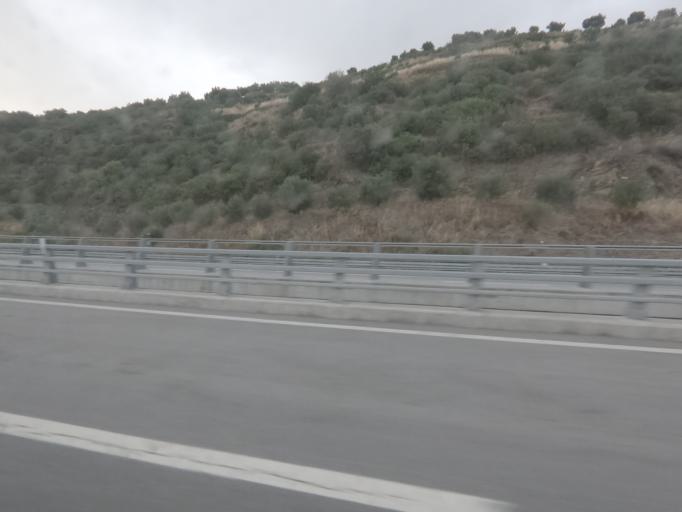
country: PT
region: Vila Real
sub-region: Peso da Regua
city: Peso da Regua
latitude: 41.1729
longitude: -7.7579
